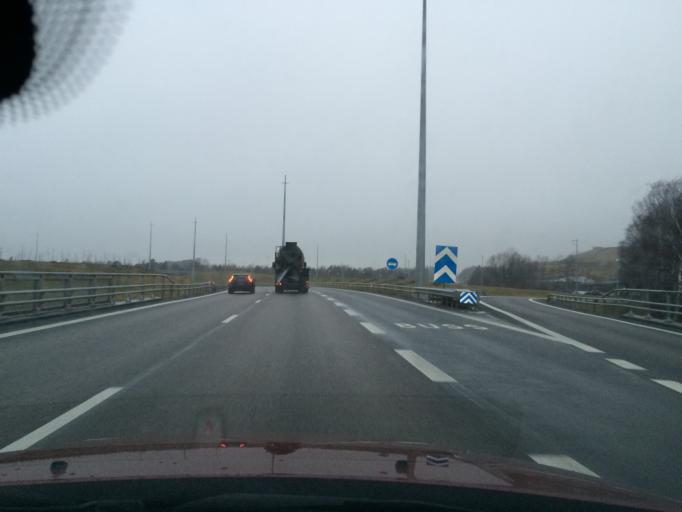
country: SE
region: Vaestra Goetaland
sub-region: Goteborg
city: Majorna
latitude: 57.7051
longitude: 11.8788
